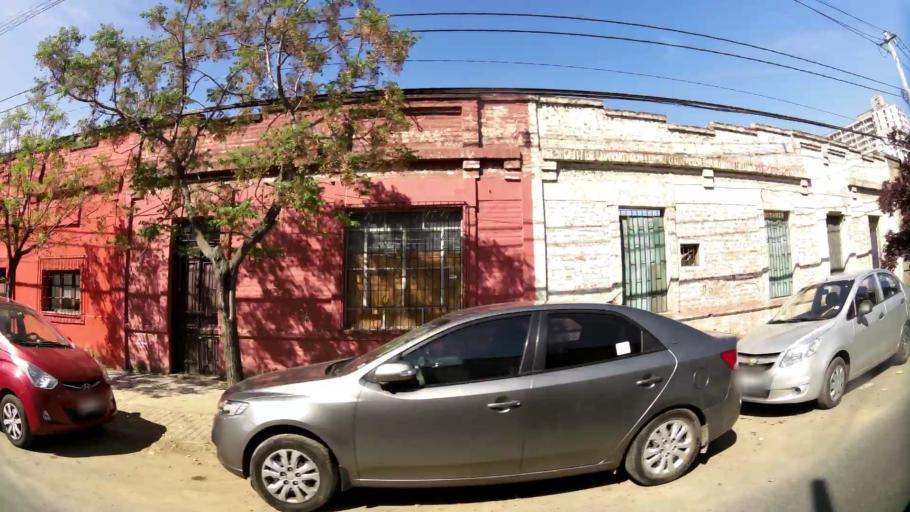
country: CL
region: Santiago Metropolitan
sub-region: Provincia de Santiago
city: Santiago
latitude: -33.4189
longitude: -70.6606
